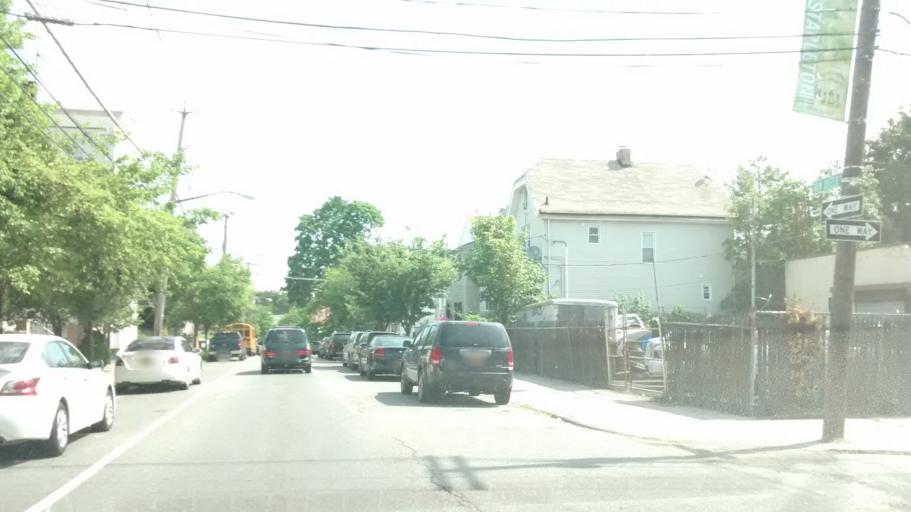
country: US
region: New Jersey
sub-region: Hudson County
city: Bayonne
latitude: 40.6295
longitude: -74.0793
